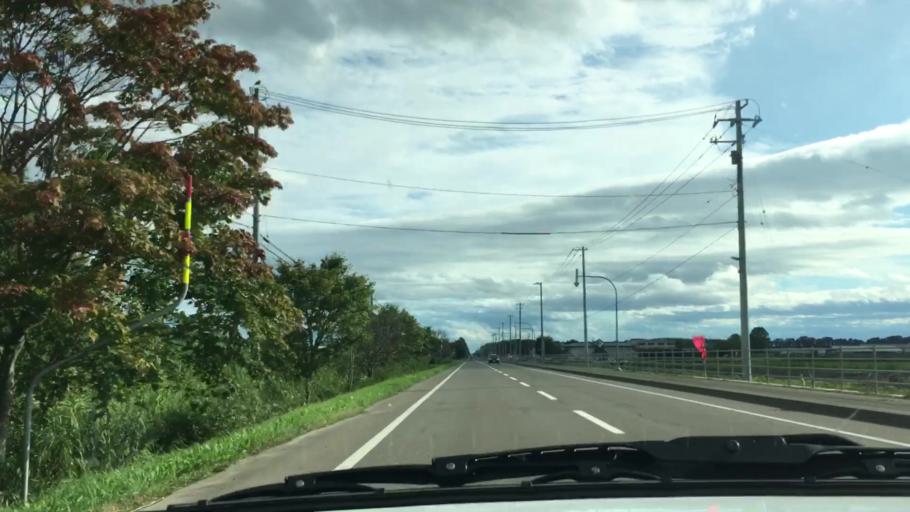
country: JP
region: Hokkaido
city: Otofuke
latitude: 43.2565
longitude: 143.3004
